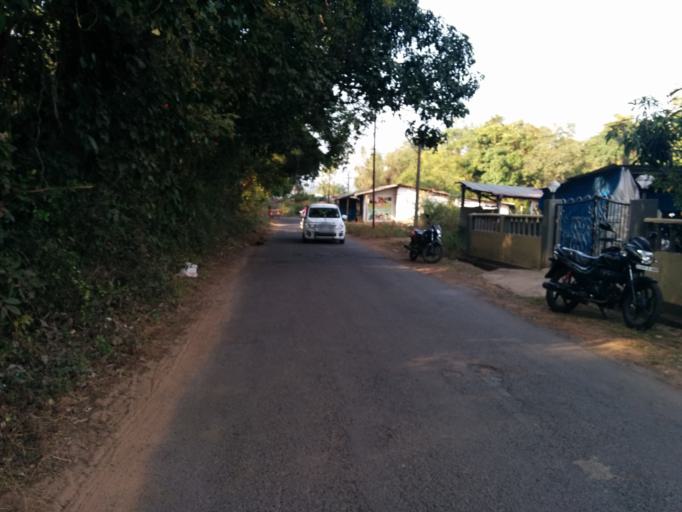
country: IN
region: Karnataka
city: Canacona
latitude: 15.0086
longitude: 74.0297
